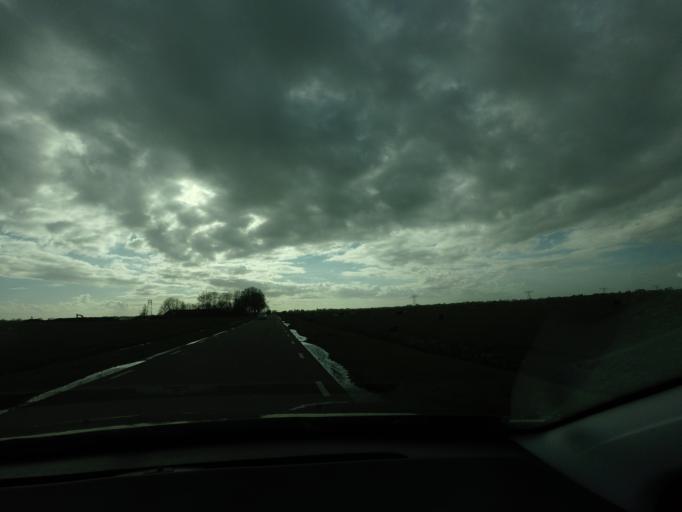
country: NL
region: Friesland
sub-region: Gemeente Boarnsterhim
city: Jirnsum
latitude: 53.0772
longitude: 5.7805
